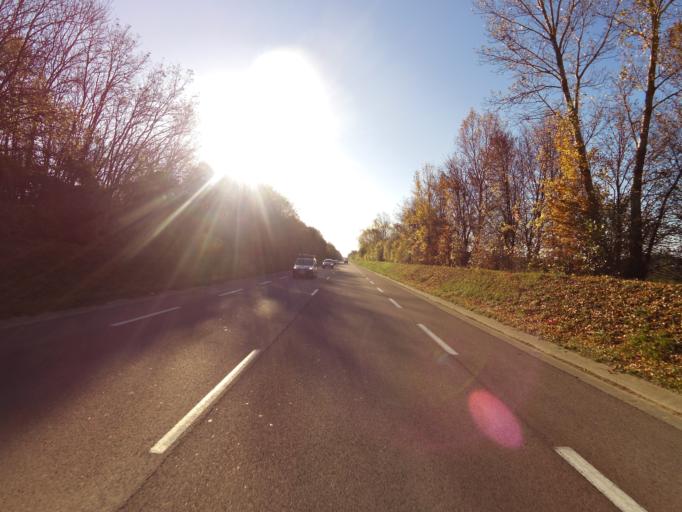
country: FR
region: Champagne-Ardenne
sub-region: Departement de l'Aube
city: Bucheres
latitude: 48.2446
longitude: 4.1175
